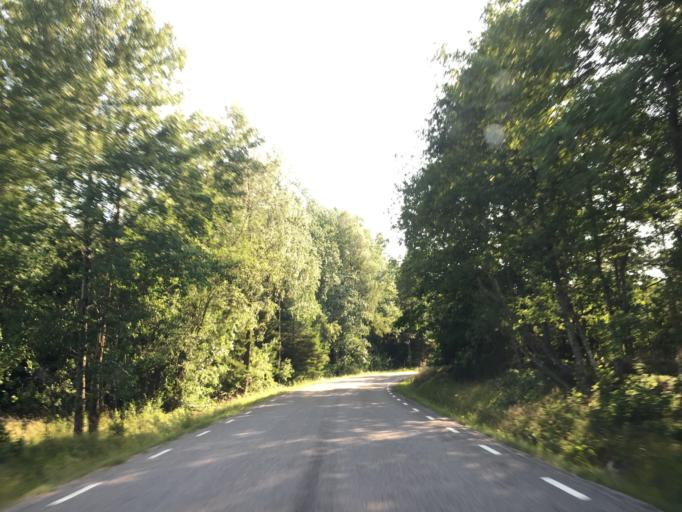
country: SE
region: Vaestra Goetaland
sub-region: Trollhattan
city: Trollhattan
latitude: 58.2663
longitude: 12.2368
